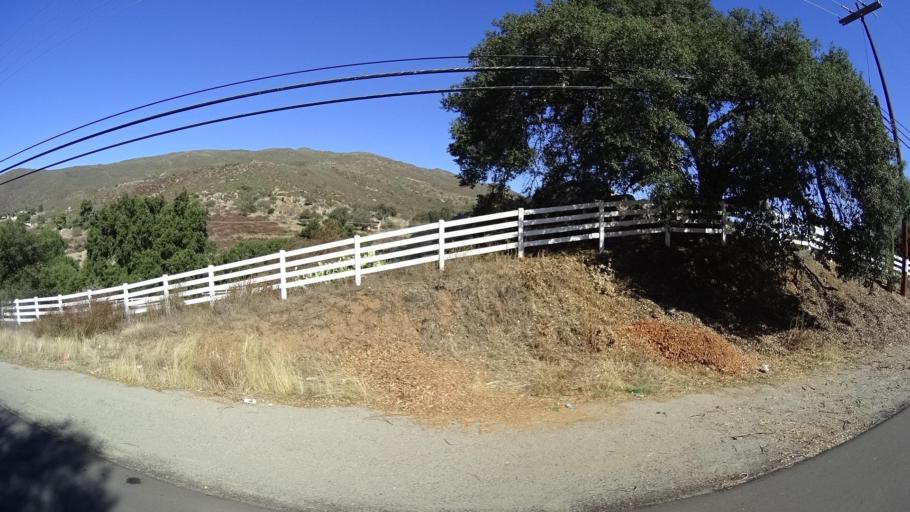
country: US
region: California
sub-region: San Diego County
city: Alpine
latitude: 32.8401
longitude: -116.7102
